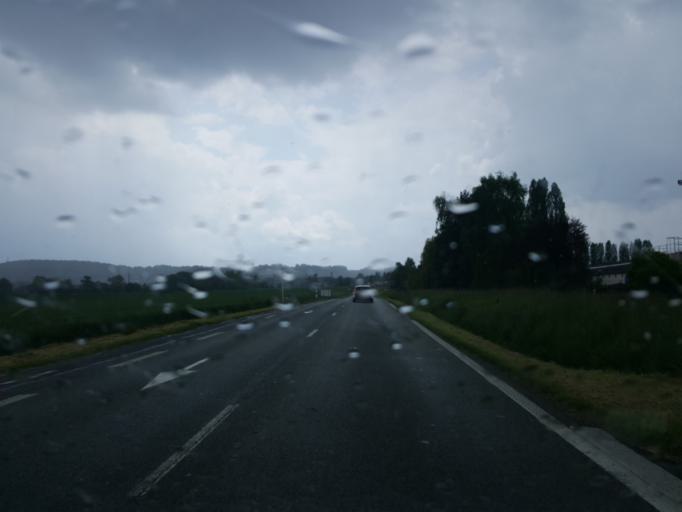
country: FR
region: Picardie
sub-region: Departement de l'Oise
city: Auneuil
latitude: 49.3866
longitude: 2.0036
